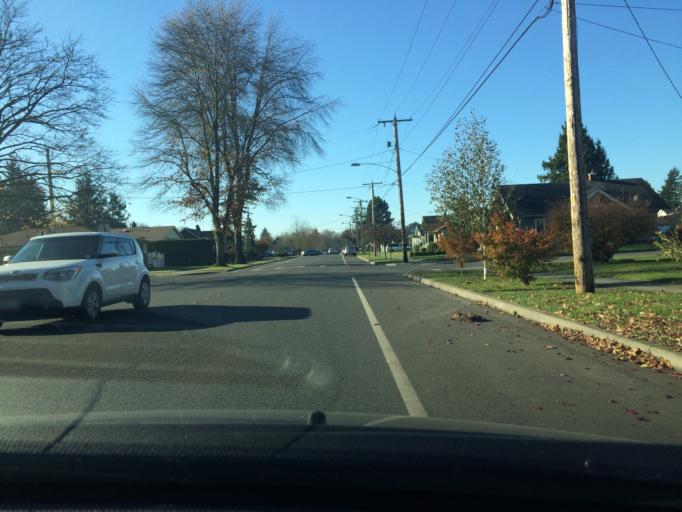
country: US
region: Washington
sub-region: Whatcom County
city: Lynden
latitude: 48.9424
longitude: -122.4582
